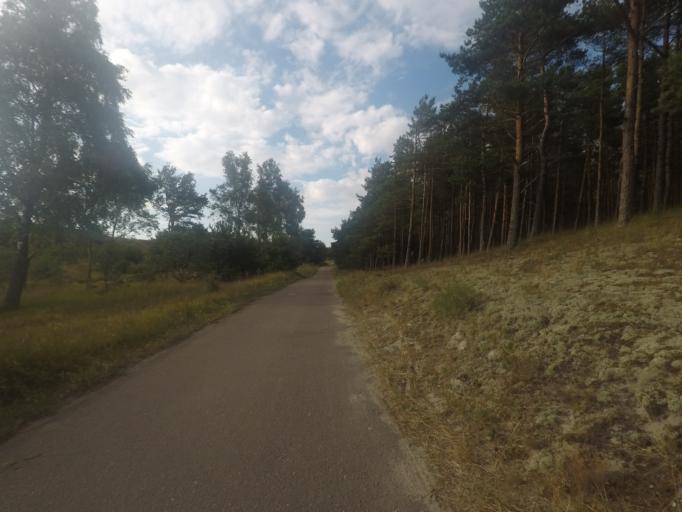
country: LT
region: Klaipedos apskritis
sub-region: Klaipeda
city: Klaipeda
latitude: 55.6833
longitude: 21.1043
